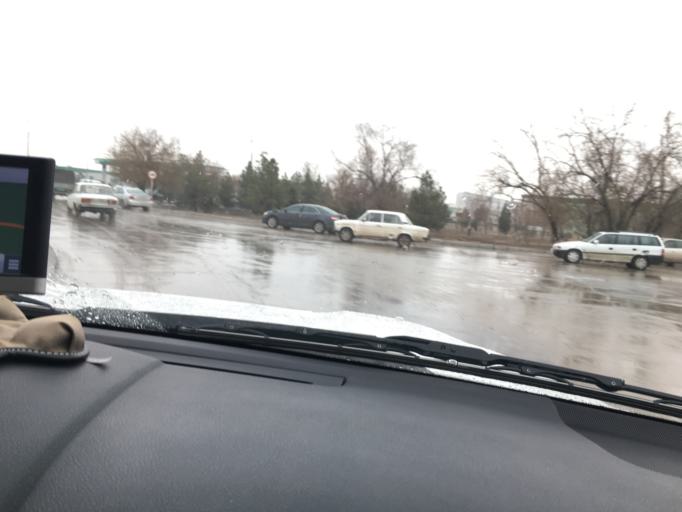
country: TM
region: Mary
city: Mary
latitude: 37.5722
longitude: 61.8333
